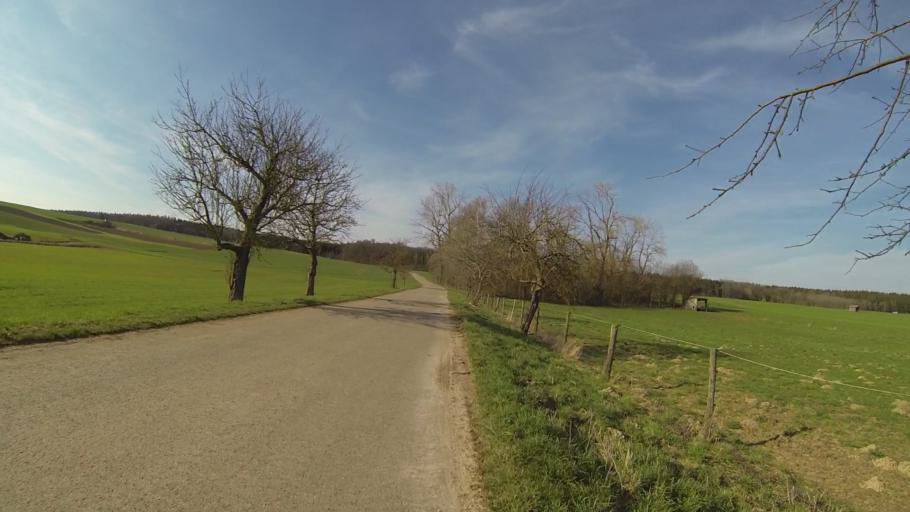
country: DE
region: Baden-Wuerttemberg
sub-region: Regierungsbezirk Stuttgart
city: Niederstotzingen
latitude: 48.5507
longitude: 10.2328
